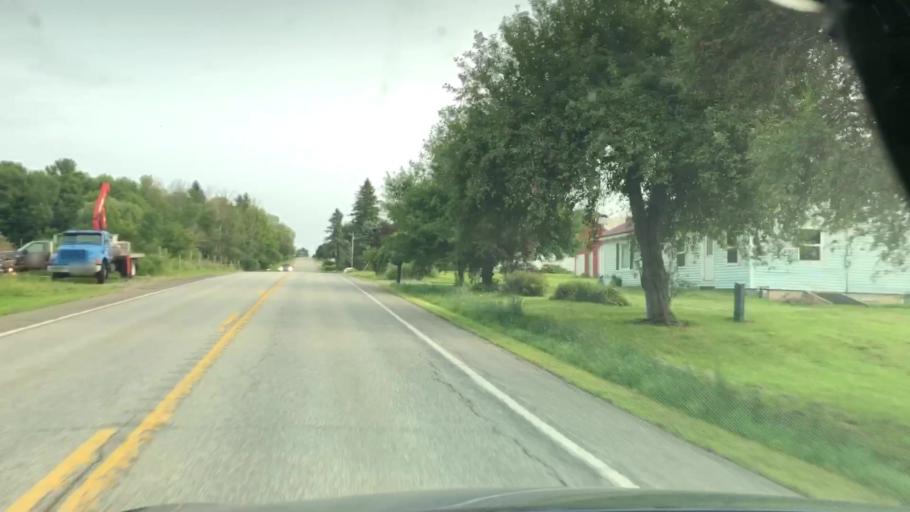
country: US
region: Pennsylvania
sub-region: Erie County
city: Union City
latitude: 41.8797
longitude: -79.8428
